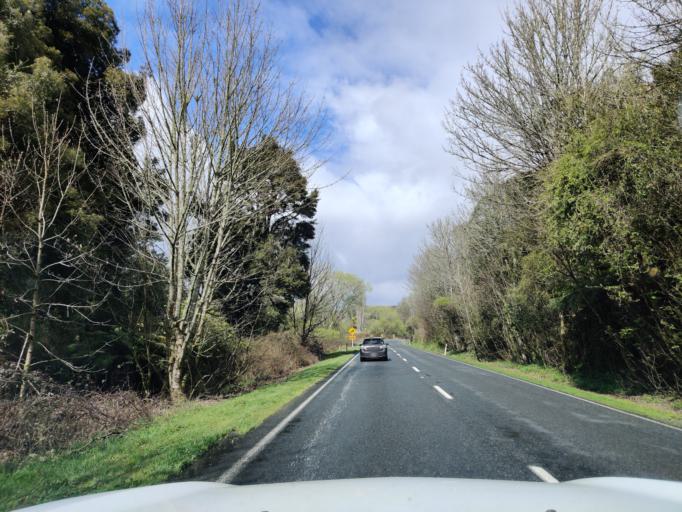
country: NZ
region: Waikato
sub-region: Otorohanga District
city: Otorohanga
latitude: -38.5953
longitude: 175.2192
